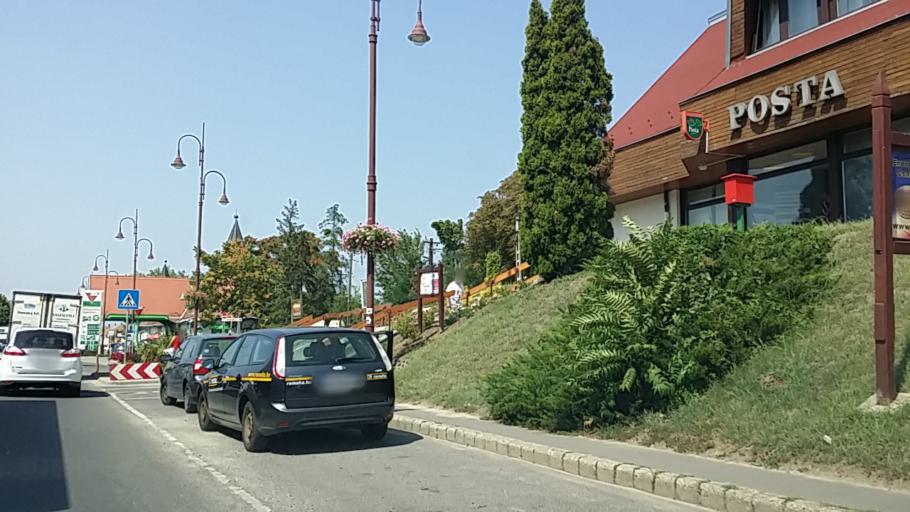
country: HU
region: Pest
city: Veresegyhaz
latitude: 47.6533
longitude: 19.2890
